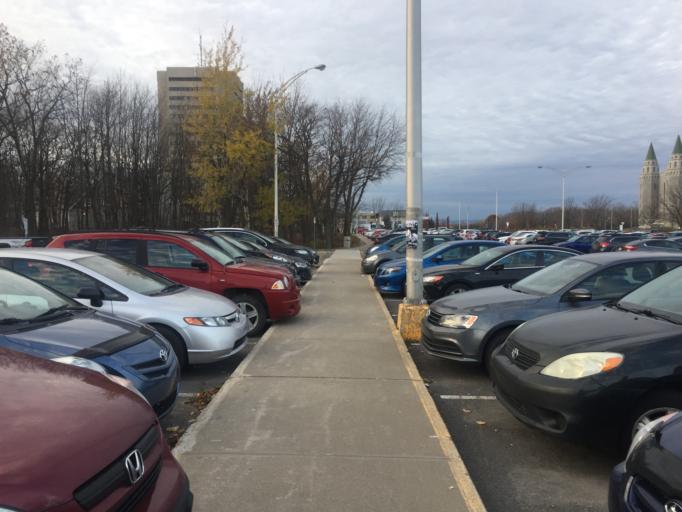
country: CA
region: Quebec
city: Quebec
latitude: 46.7799
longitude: -71.2705
